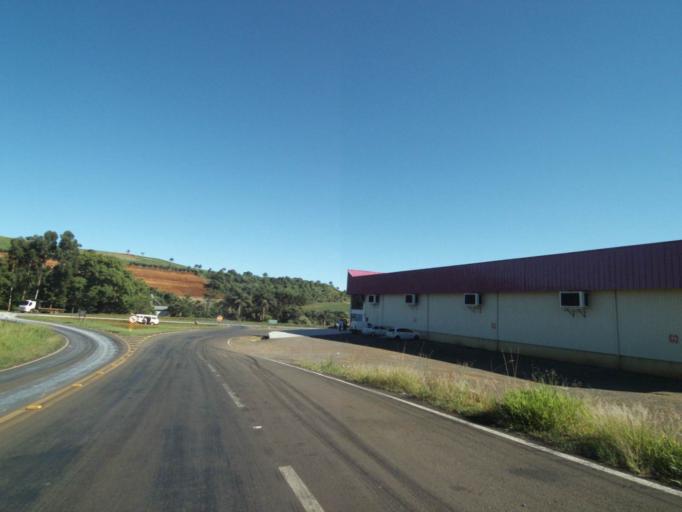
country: BR
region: Santa Catarina
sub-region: Sao Lourenco Do Oeste
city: Sao Lourenco dOeste
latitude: -26.2590
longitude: -52.7871
